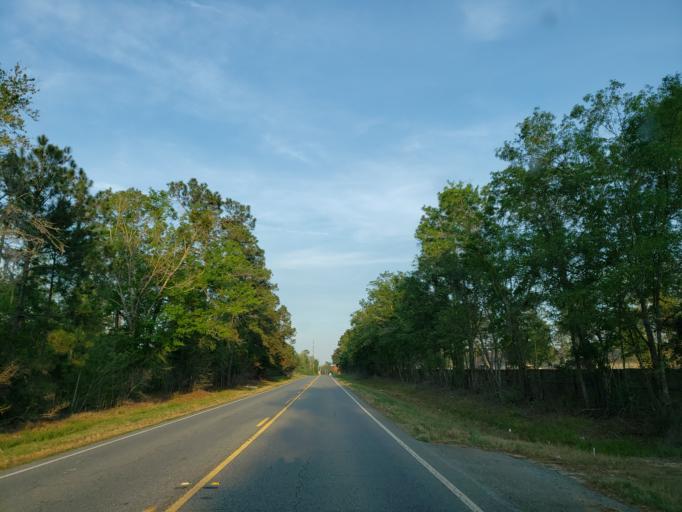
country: US
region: Georgia
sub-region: Lowndes County
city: Hahira
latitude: 30.9949
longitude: -83.4053
